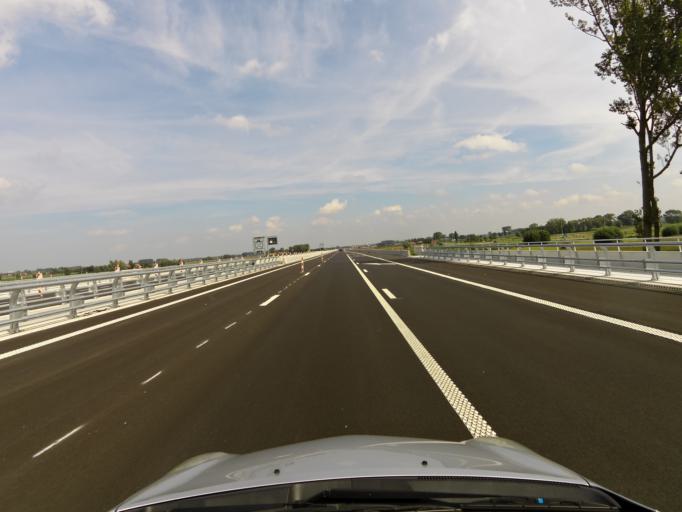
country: BE
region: Flanders
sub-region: Provincie West-Vlaanderen
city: Damme
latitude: 51.2974
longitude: 3.2599
